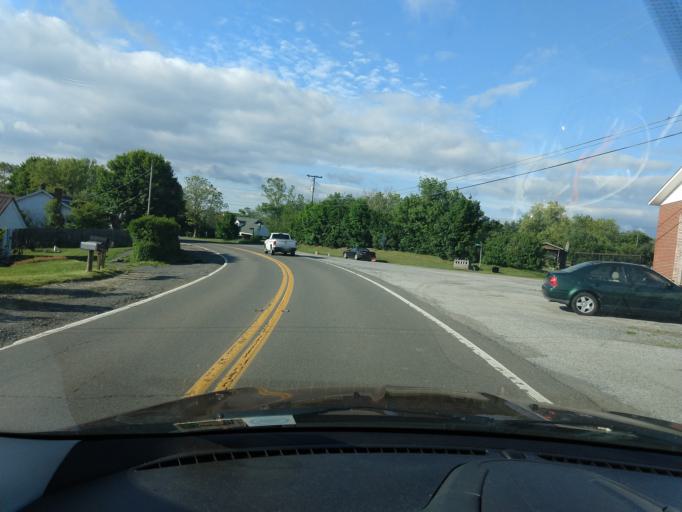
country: US
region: Virginia
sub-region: City of Galax
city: Galax
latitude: 36.7312
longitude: -80.9814
